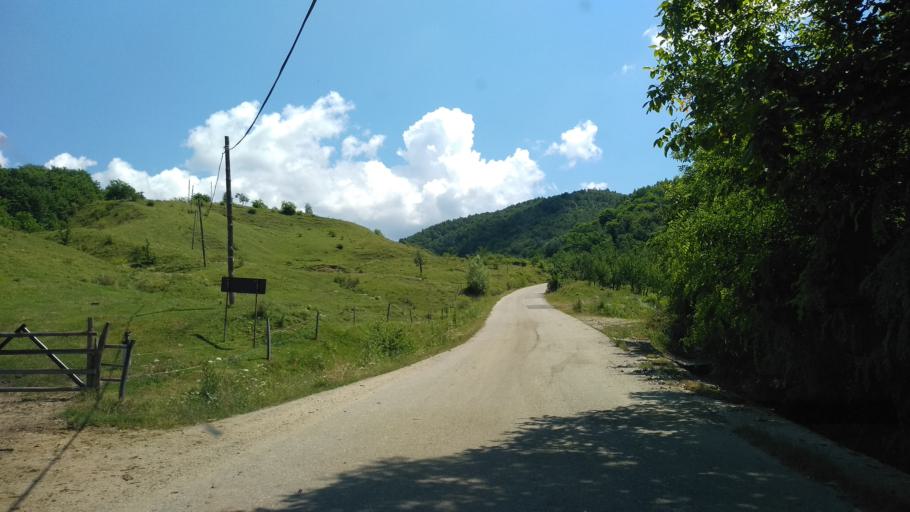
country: RO
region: Hunedoara
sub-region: Comuna Orastioara de Sus
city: Orastioara de Sus
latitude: 45.7081
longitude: 23.1384
